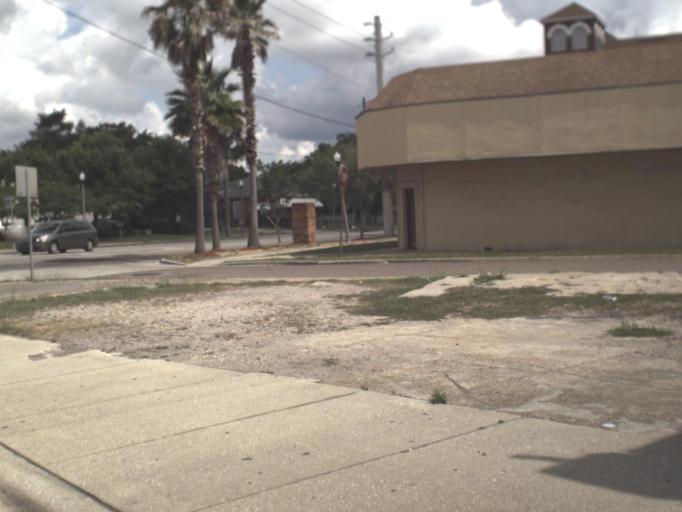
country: US
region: Florida
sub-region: Duval County
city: Jacksonville
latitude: 30.3407
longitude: -81.6752
